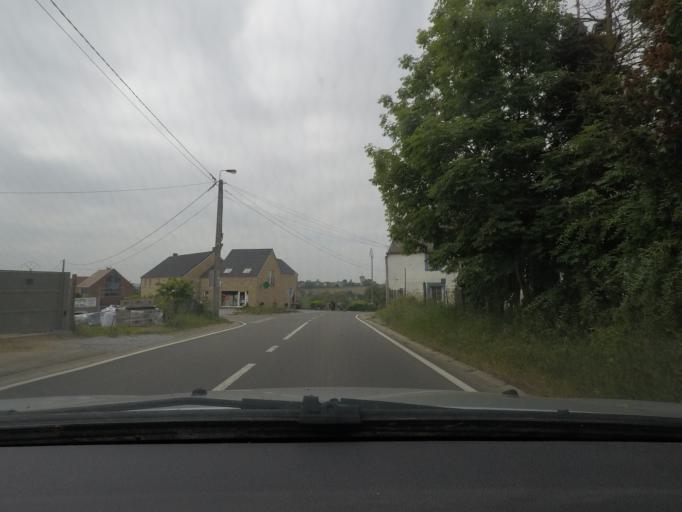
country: BE
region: Wallonia
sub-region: Province de Namur
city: Noville-les-Bois
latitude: 50.5046
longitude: 5.0041
